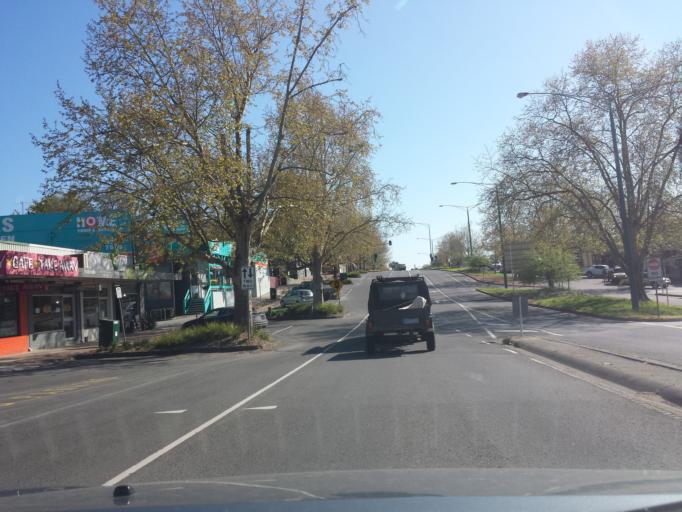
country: AU
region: Victoria
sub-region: Yarra Ranges
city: Yarra Glen
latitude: -37.6597
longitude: 145.3740
